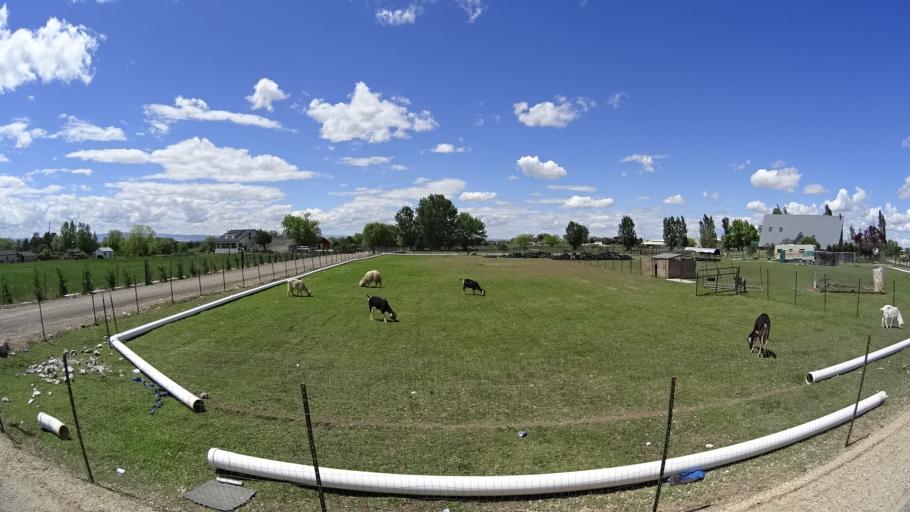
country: US
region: Idaho
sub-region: Ada County
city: Kuna
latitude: 43.5586
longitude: -116.4536
